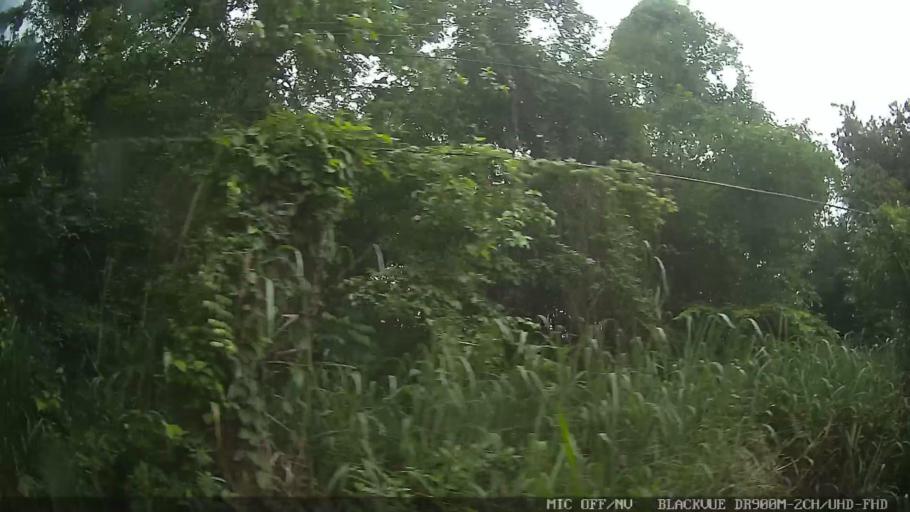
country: BR
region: Sao Paulo
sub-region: Pedreira
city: Pedreira
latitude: -22.6891
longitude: -46.8799
